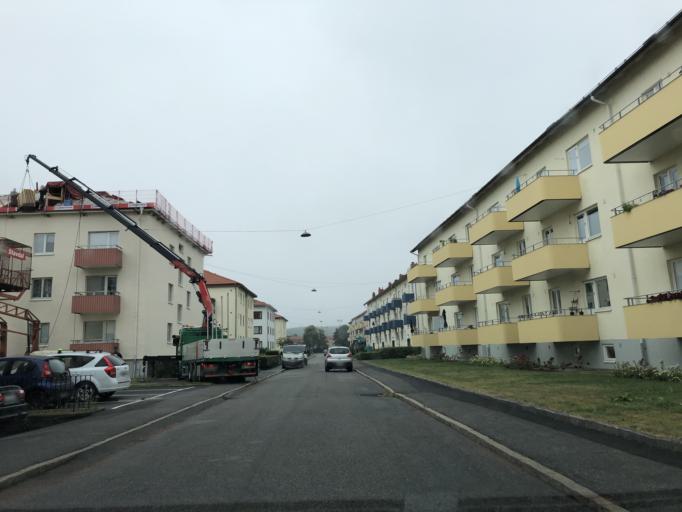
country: SE
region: Vaestra Goetaland
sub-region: Goteborg
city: Majorna
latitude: 57.7301
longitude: 11.9318
